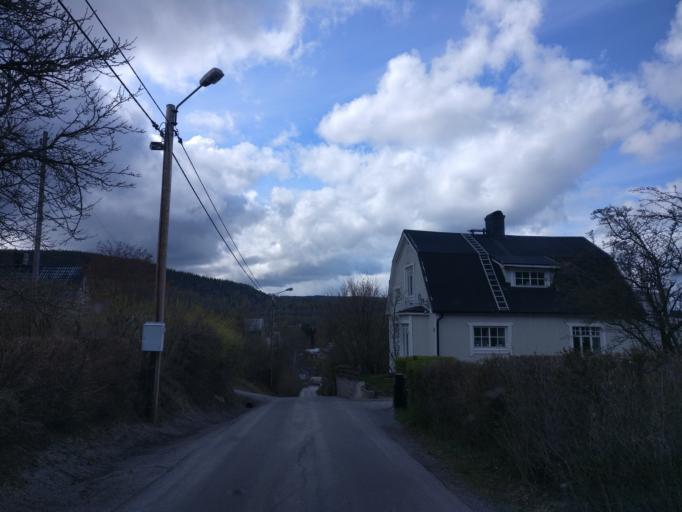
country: SE
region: Vaesternorrland
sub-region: Sundsvalls Kommun
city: Skottsund
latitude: 62.3065
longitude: 17.3908
